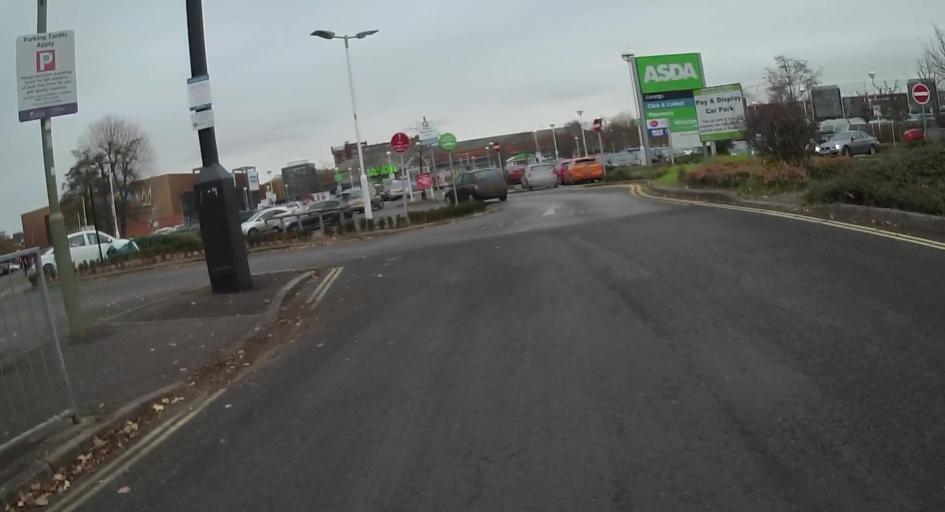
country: GB
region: England
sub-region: Hampshire
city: Farnborough
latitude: 51.2907
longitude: -0.7610
